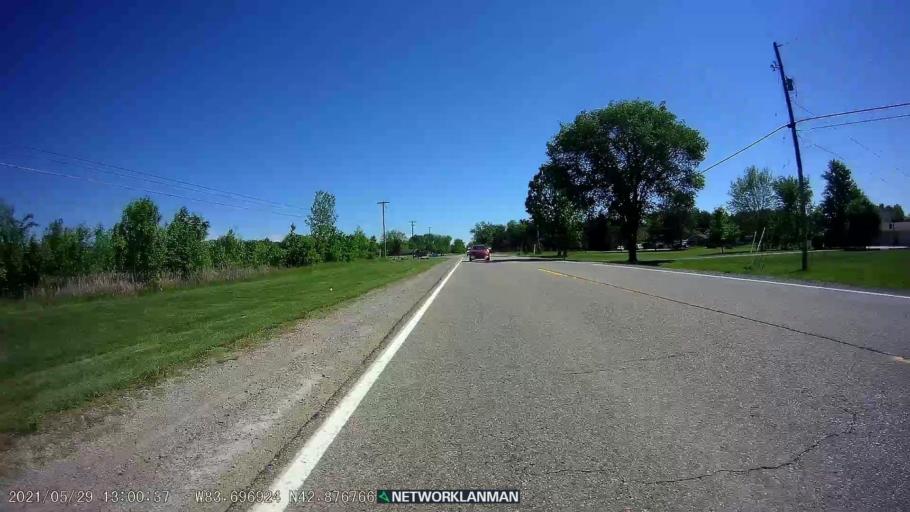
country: US
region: Michigan
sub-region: Genesee County
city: Lake Fenton
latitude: 42.8769
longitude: -83.6969
